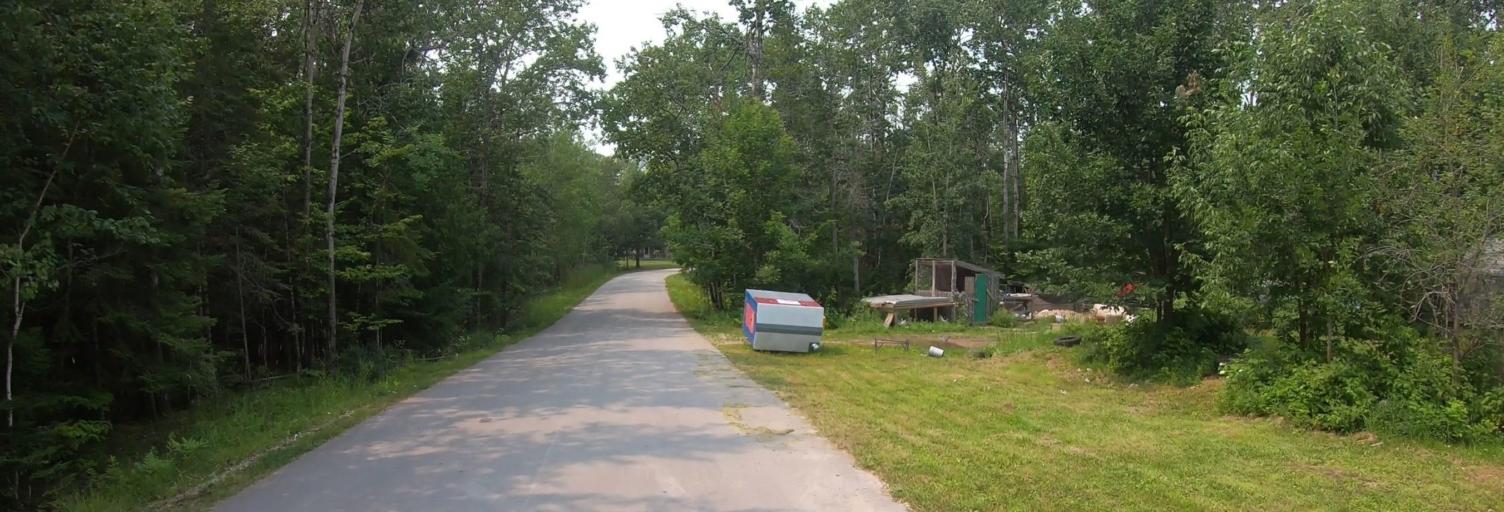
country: CA
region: Ontario
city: Thessalon
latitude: 46.0313
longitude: -83.6775
